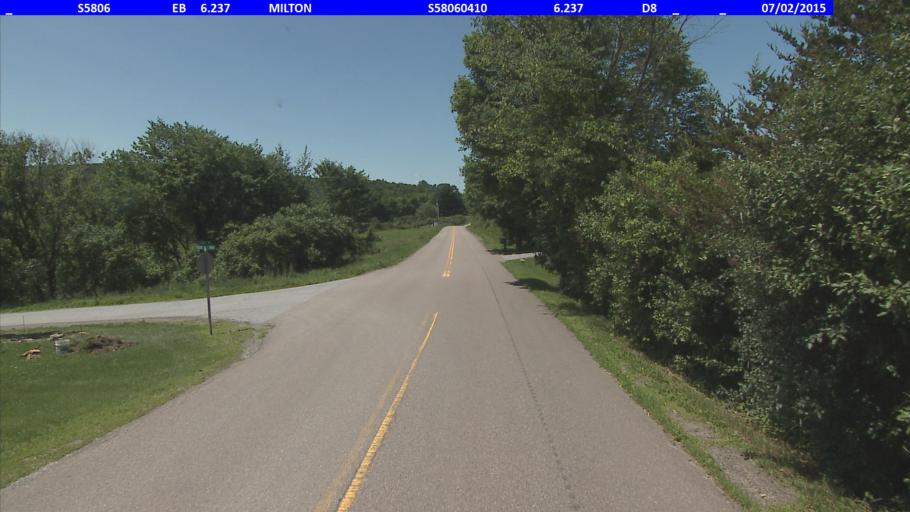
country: US
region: Vermont
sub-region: Chittenden County
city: Milton
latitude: 44.7044
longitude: -73.1891
